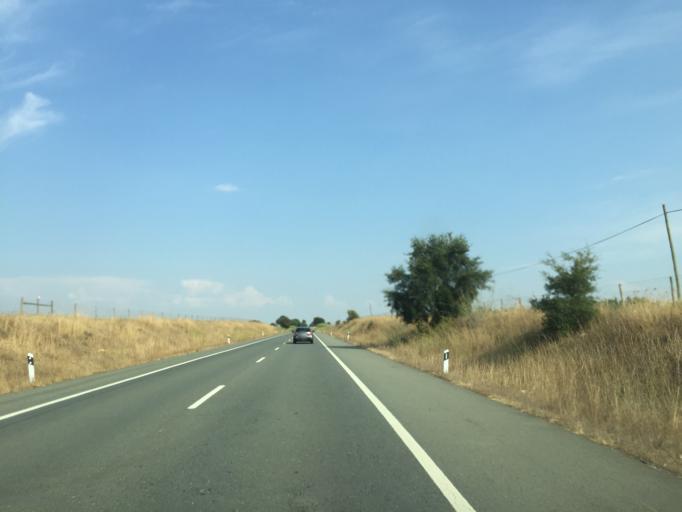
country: PT
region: Beja
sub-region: Aljustrel
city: Aljustrel
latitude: 37.9396
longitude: -8.3701
